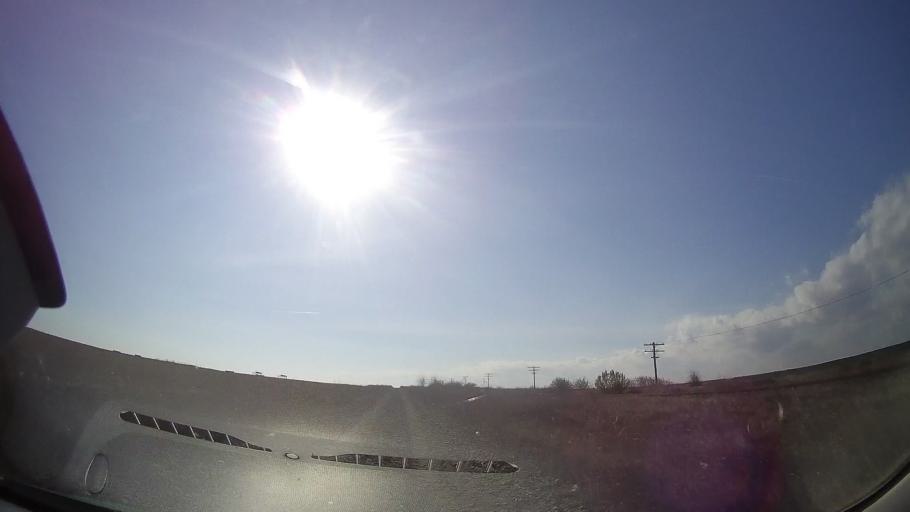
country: RO
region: Constanta
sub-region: Comuna Costinesti
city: Schitu
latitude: 43.9206
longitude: 28.6303
